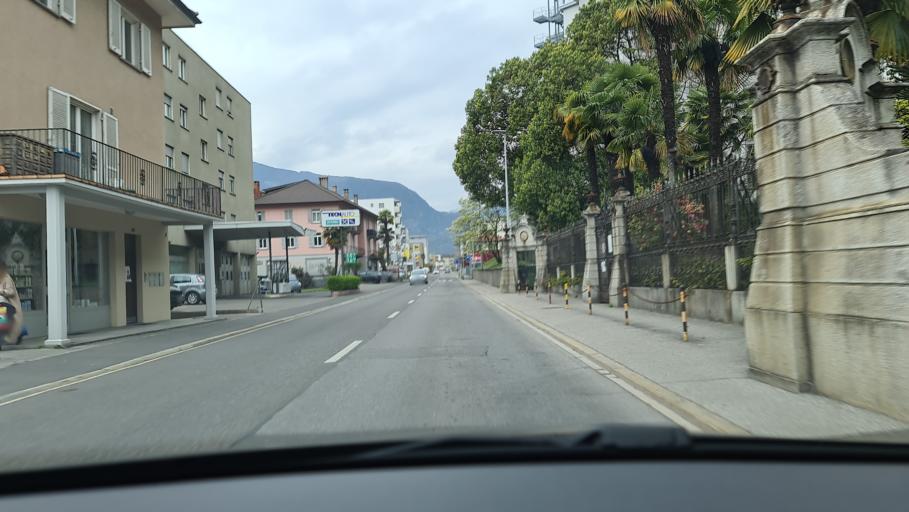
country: CH
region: Ticino
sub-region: Locarno District
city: Locarno
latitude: 46.1698
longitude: 8.7857
